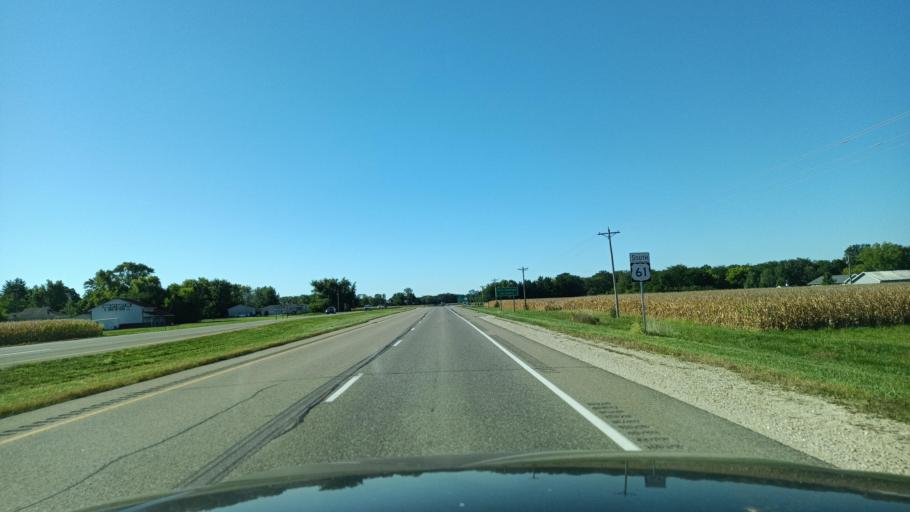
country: US
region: Iowa
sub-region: Lee County
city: Fort Madison
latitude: 40.6867
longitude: -91.2504
